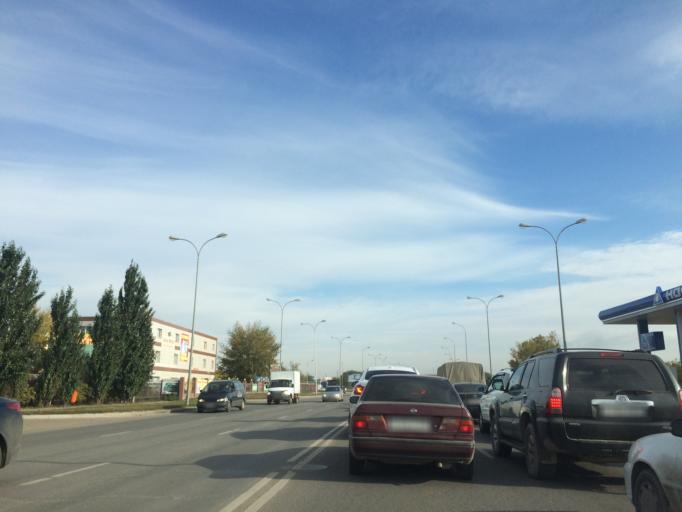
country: KZ
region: Astana Qalasy
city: Astana
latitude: 51.1668
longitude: 71.4766
